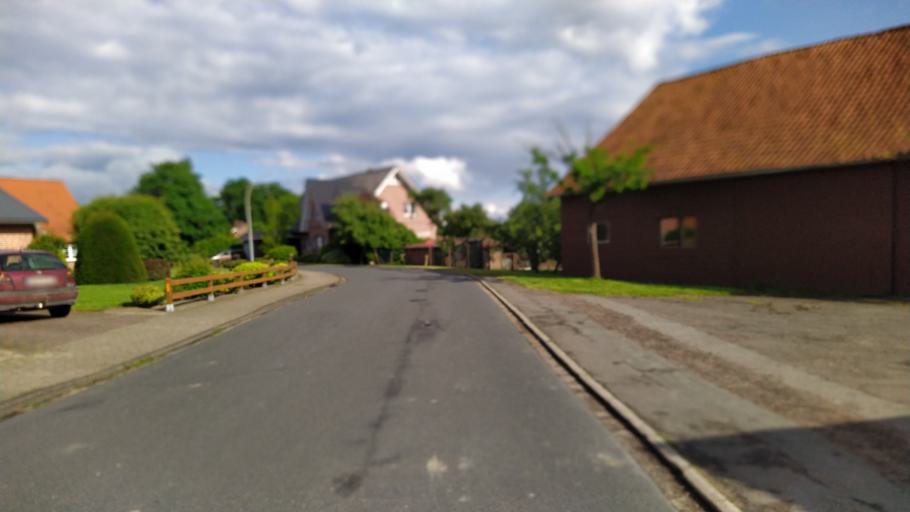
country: DE
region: Lower Saxony
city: Bremervorde
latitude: 53.4394
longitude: 9.1785
